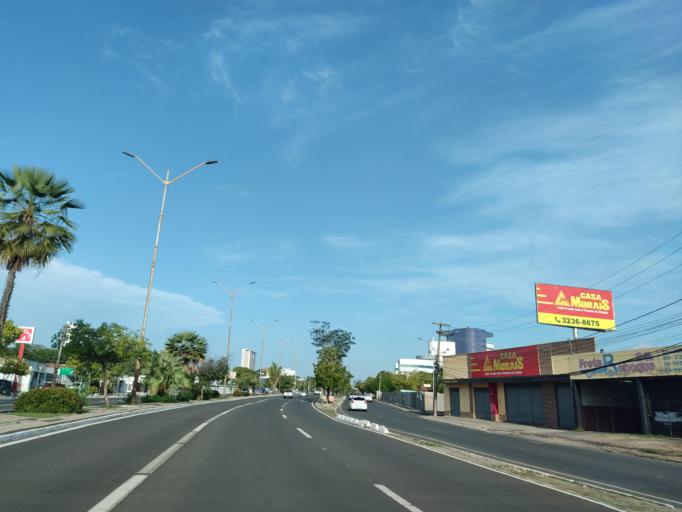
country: BR
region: Piaui
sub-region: Teresina
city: Teresina
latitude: -5.0803
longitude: -42.7890
